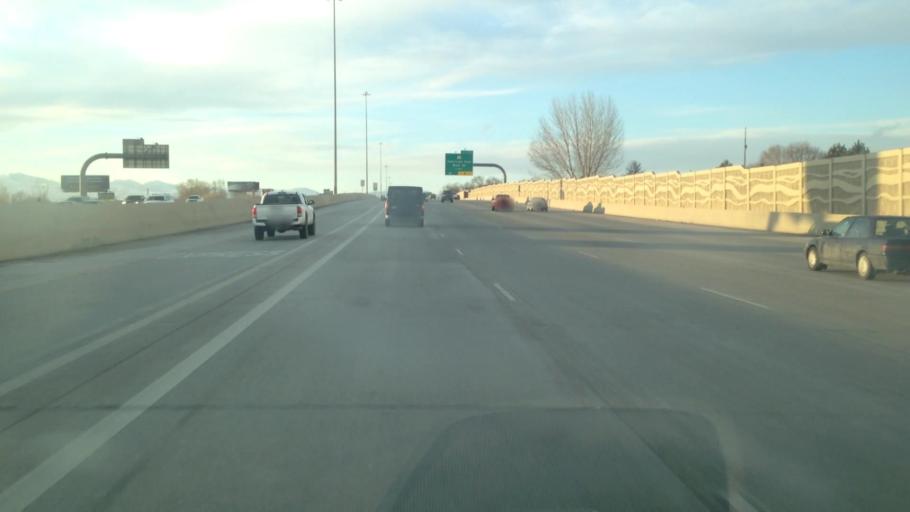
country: US
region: Utah
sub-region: Utah County
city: American Fork
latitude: 40.3650
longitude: -111.7922
